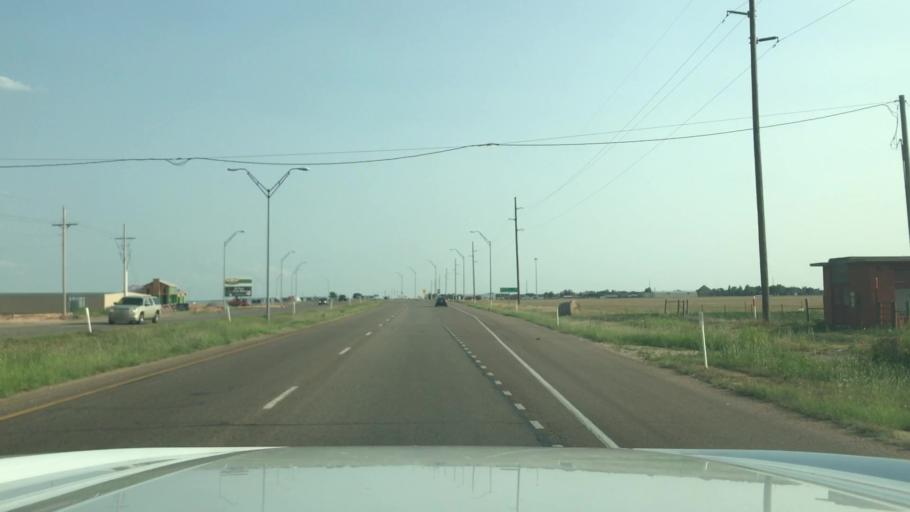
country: US
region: Texas
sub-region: Potter County
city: Bushland
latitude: 35.1251
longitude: -101.9381
